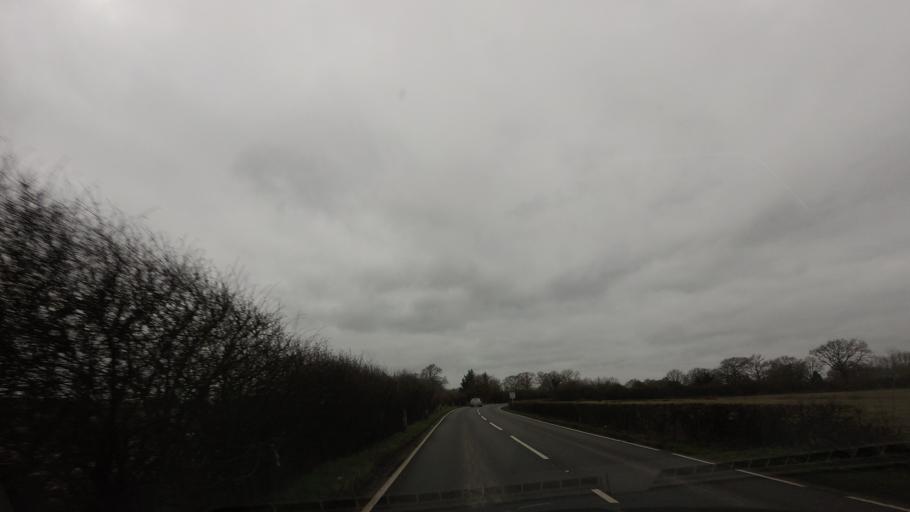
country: GB
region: England
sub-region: Kent
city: Staplehurst
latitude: 51.1923
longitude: 0.5362
